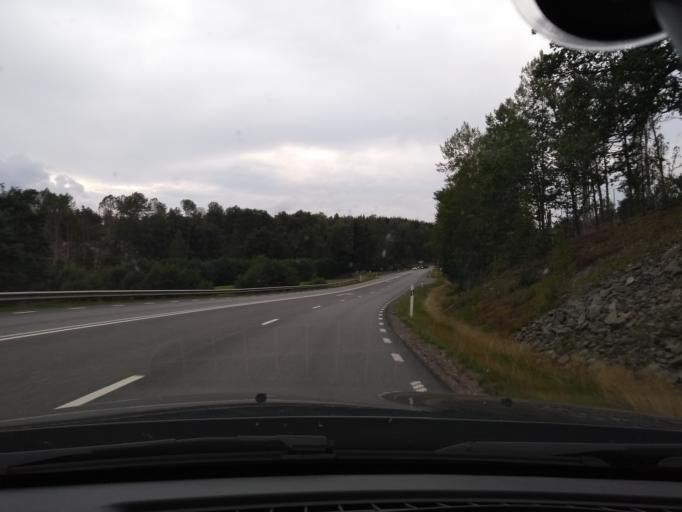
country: SE
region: Joenkoeping
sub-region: Eksjo Kommun
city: Eksjoe
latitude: 57.6357
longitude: 14.8503
